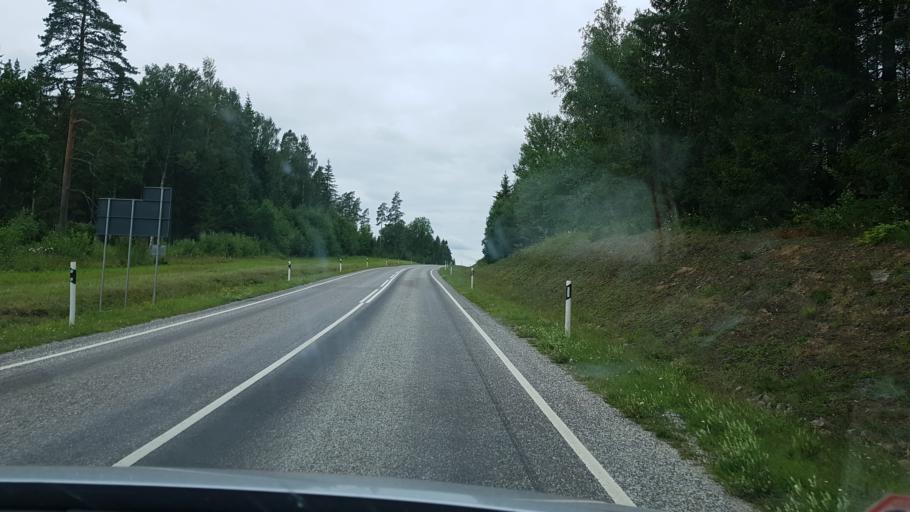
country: EE
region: Vorumaa
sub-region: Antsla vald
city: Vana-Antsla
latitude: 57.9982
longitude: 26.7215
